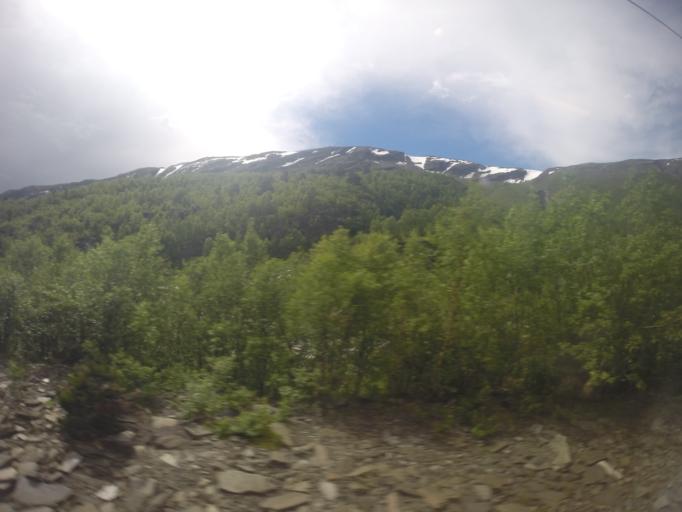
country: NO
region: Sor-Trondelag
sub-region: Oppdal
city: Oppdal
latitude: 62.4710
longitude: 9.5746
